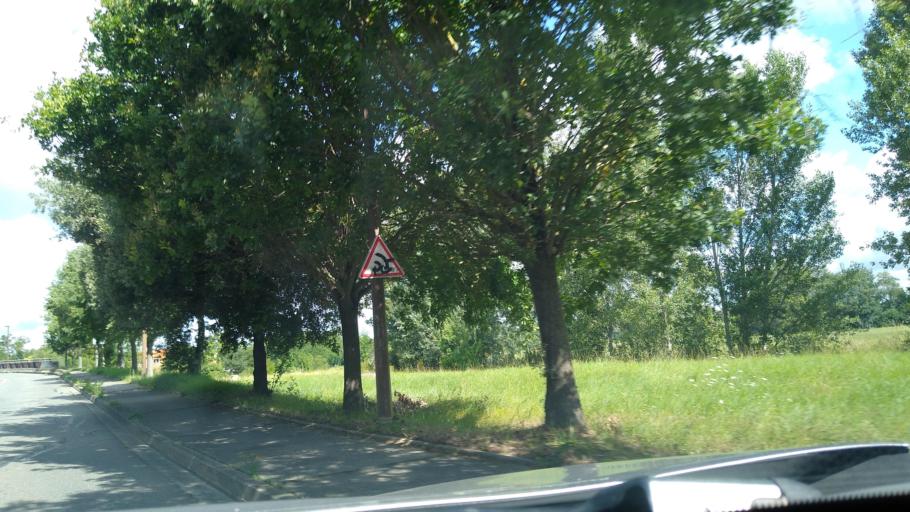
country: FR
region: Midi-Pyrenees
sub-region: Departement de la Haute-Garonne
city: L'Union
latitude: 43.6386
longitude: 1.4794
